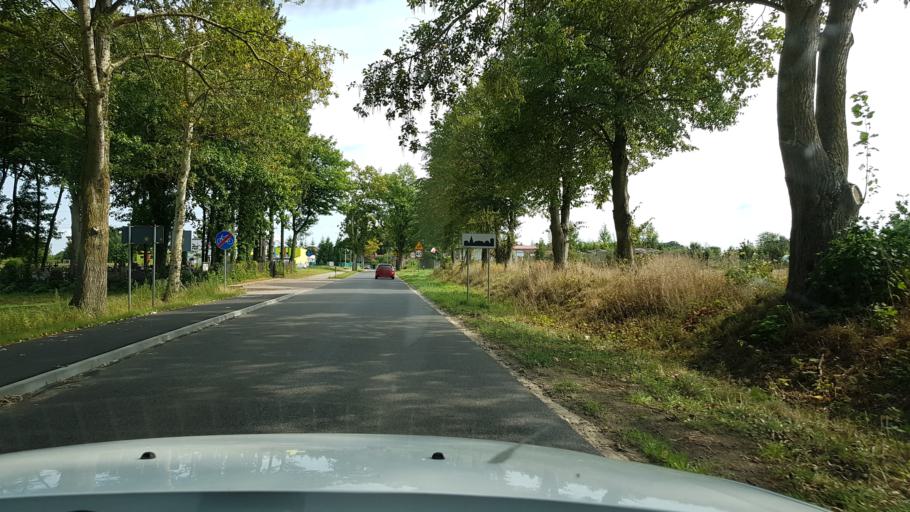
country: PL
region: West Pomeranian Voivodeship
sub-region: Powiat koszalinski
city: Sianow
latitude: 54.2607
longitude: 16.2605
